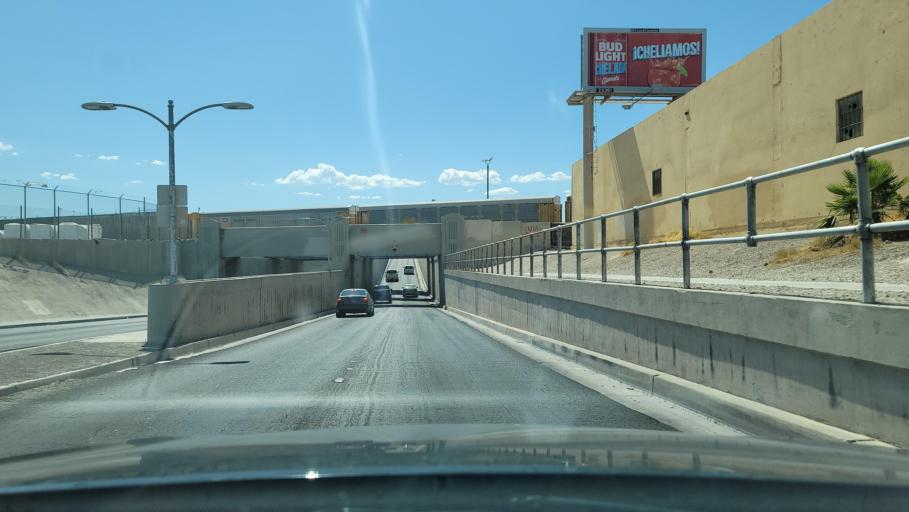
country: US
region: Nevada
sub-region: Clark County
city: Las Vegas
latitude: 36.1774
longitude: -115.1434
